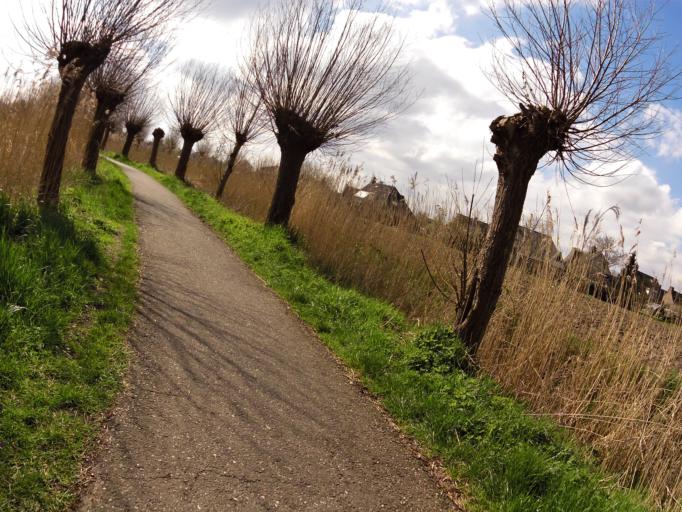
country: NL
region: North Brabant
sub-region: Gemeente Boxtel
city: Boxtel
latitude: 51.6099
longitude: 5.2959
